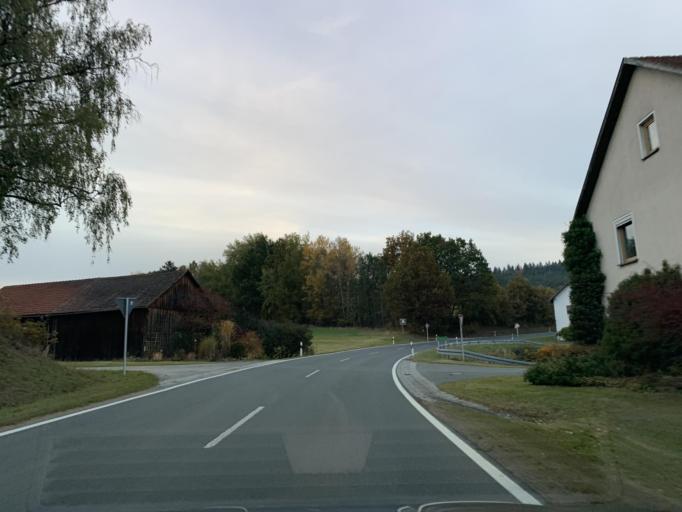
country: DE
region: Bavaria
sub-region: Upper Palatinate
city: Bach
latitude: 49.3771
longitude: 12.3759
